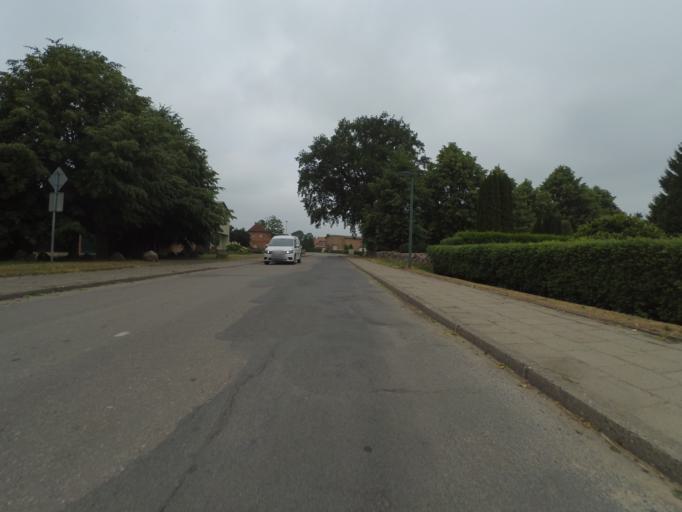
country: DE
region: Mecklenburg-Vorpommern
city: Plau am See
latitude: 53.4970
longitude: 12.2114
